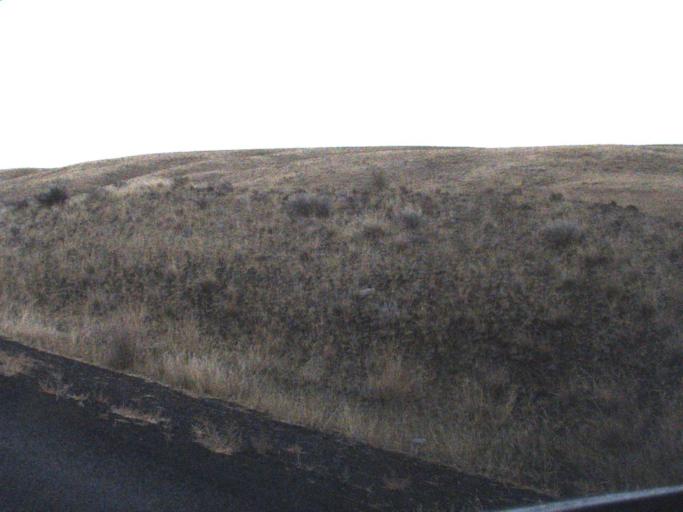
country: US
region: Washington
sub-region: Garfield County
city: Pomeroy
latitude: 46.7846
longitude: -117.9230
